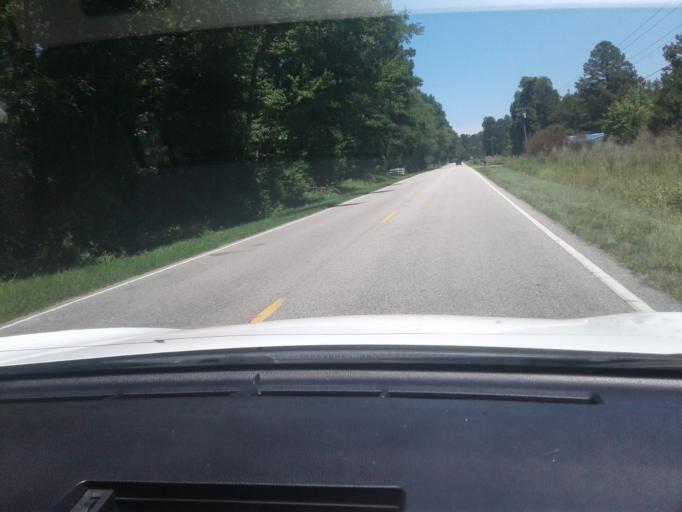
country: US
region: North Carolina
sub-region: Harnett County
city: Erwin
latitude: 35.3176
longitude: -78.7139
